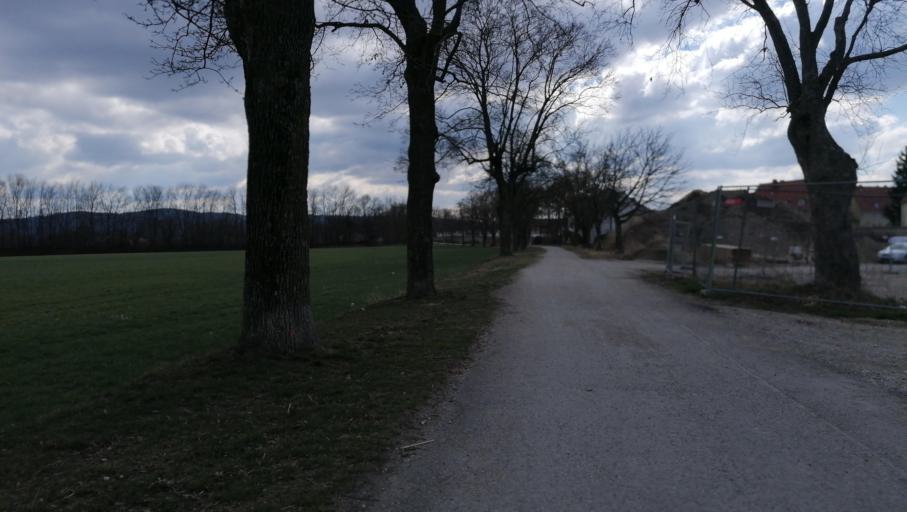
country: AT
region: Lower Austria
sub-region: Wiener Neustadt Stadt
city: Wiener Neustadt
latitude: 47.7985
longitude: 16.2427
